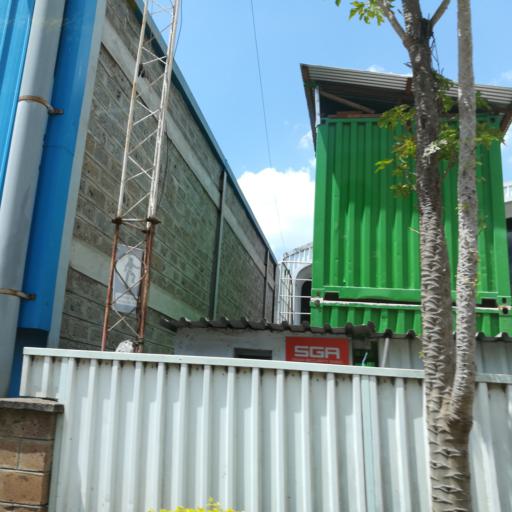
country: KE
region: Nairobi Area
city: Nairobi
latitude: -1.3191
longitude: 36.8172
